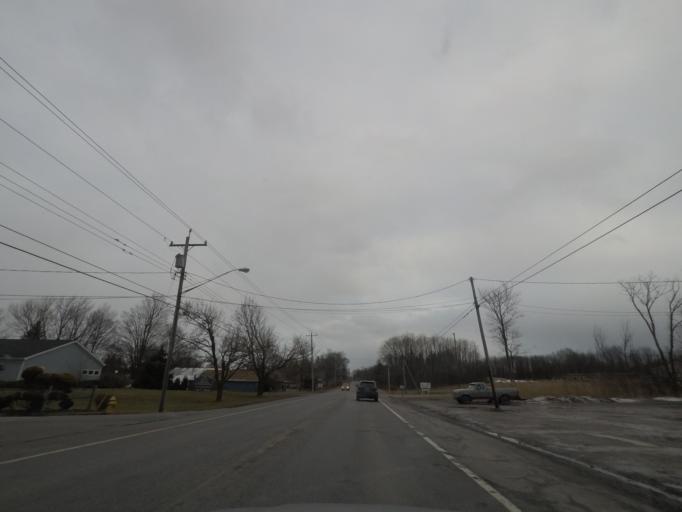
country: US
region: New York
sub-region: Madison County
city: Wampsville
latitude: 43.0746
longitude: -75.7151
